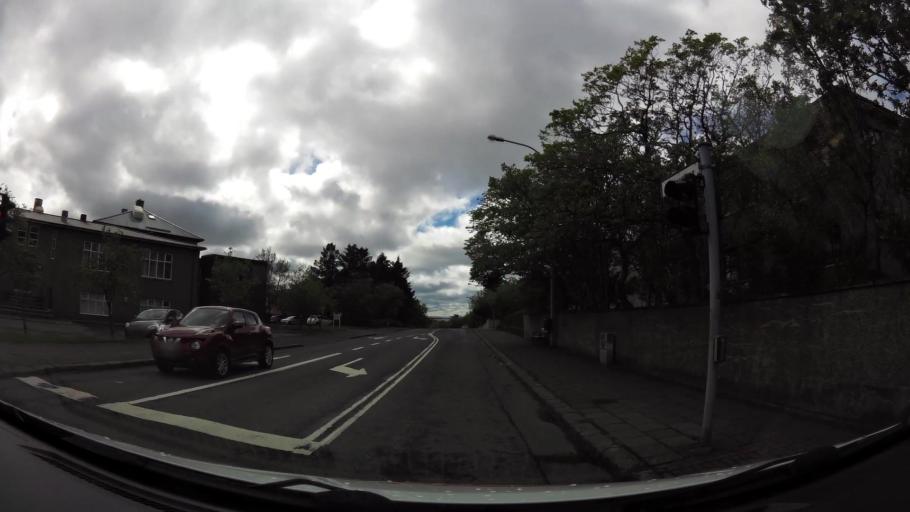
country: IS
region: Capital Region
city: Kopavogur
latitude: 64.1402
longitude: -21.9263
